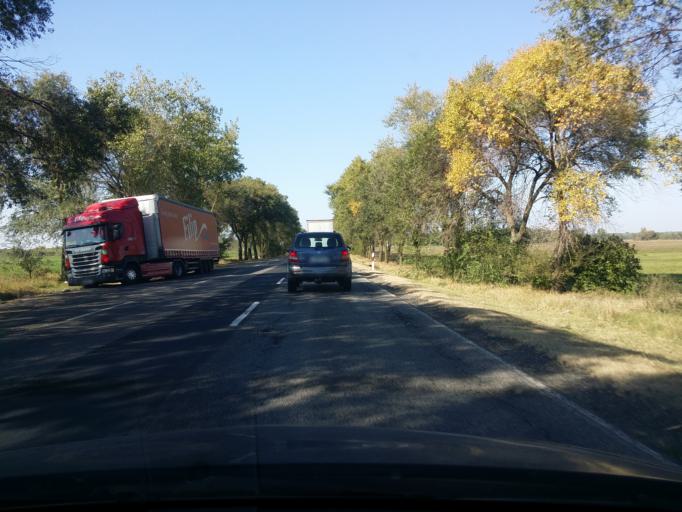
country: HU
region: Bacs-Kiskun
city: Nyarlorinc
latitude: 46.9113
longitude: 19.8049
